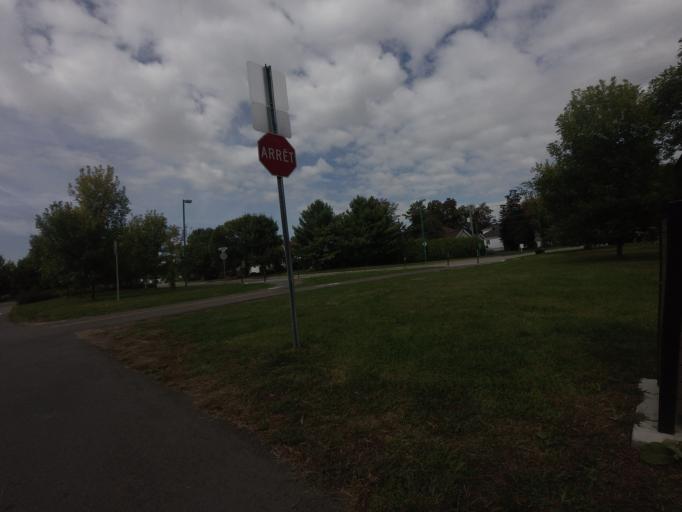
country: CA
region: Quebec
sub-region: Laurentides
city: Blainville
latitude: 45.6879
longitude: -73.8861
